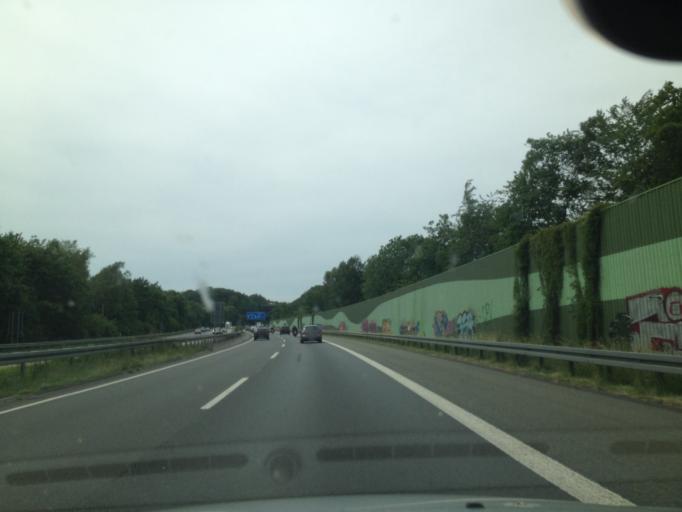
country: DE
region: North Rhine-Westphalia
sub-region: Regierungsbezirk Arnsberg
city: Luedenscheid
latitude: 51.2549
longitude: 7.6150
